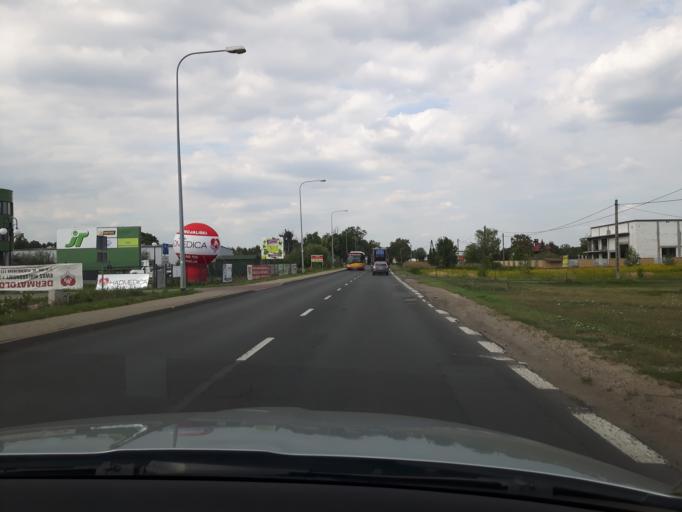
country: PL
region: Masovian Voivodeship
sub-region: Powiat legionowski
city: Stanislawow Pierwszy
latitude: 52.3407
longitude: 21.0288
